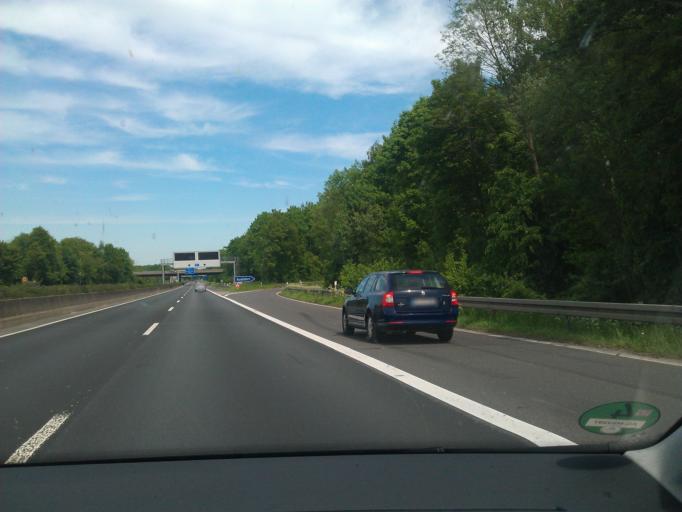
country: DE
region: North Rhine-Westphalia
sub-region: Regierungsbezirk Dusseldorf
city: Neubrueck
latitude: 51.1624
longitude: 6.6455
